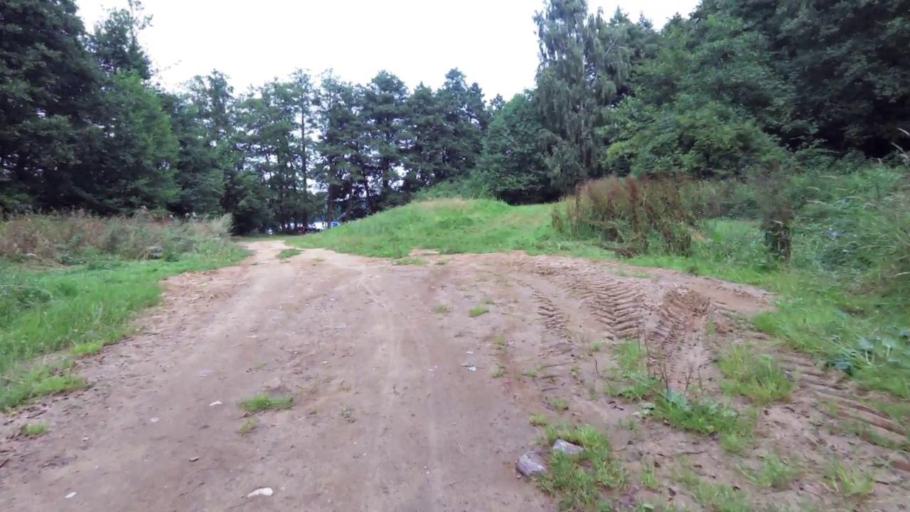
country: PL
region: West Pomeranian Voivodeship
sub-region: Powiat drawski
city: Czaplinek
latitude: 53.5805
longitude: 16.2558
